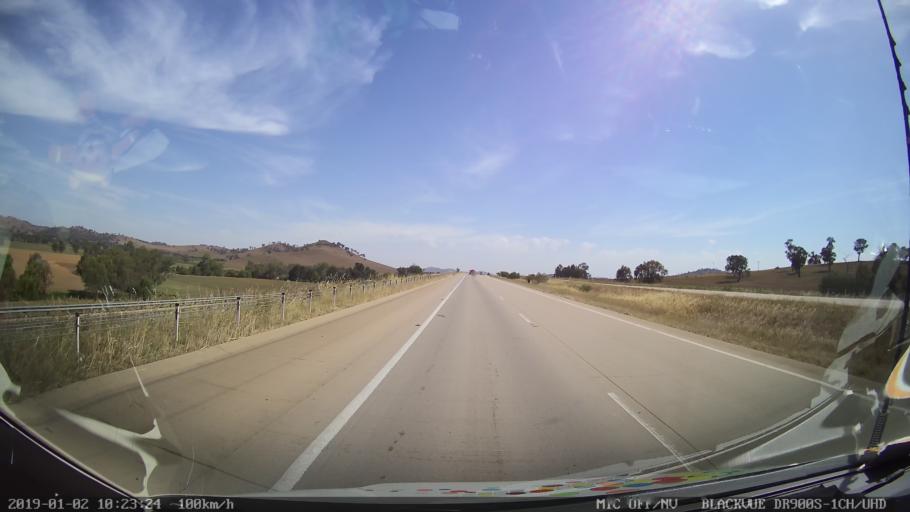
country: AU
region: New South Wales
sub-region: Gundagai
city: Gundagai
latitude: -34.9596
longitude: 148.1568
